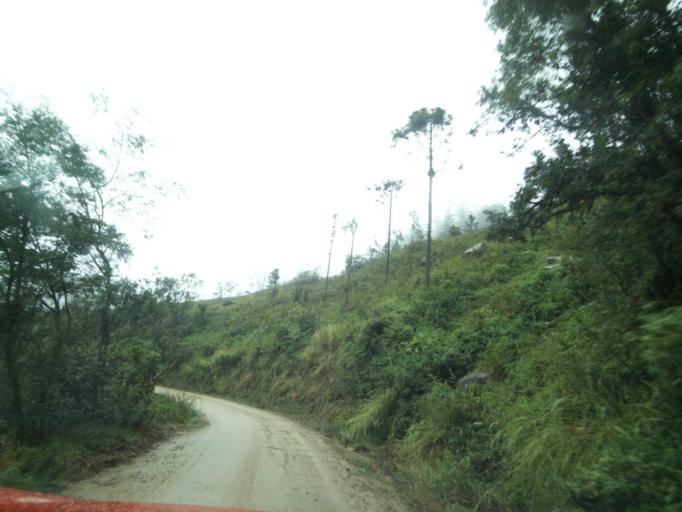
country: BR
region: Santa Catarina
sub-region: Anitapolis
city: Anitapolis
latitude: -27.9072
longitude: -49.1948
